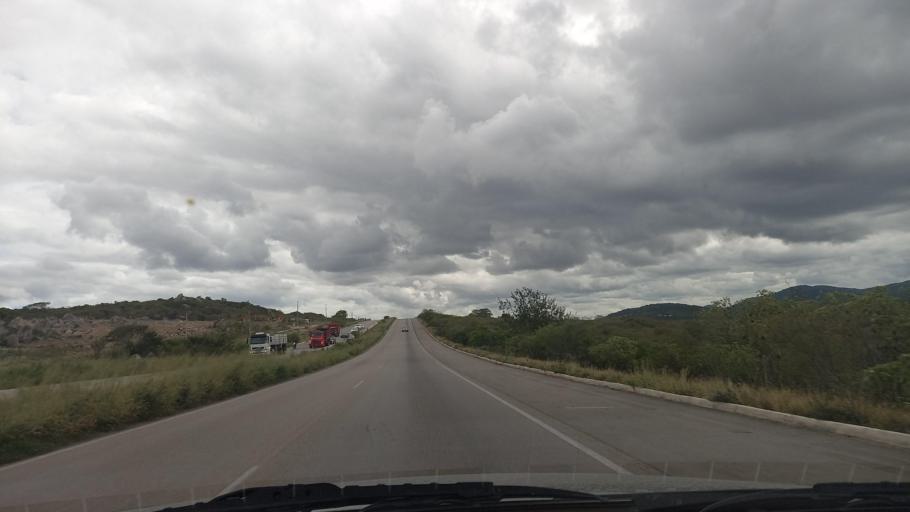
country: BR
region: Pernambuco
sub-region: Caruaru
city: Caruaru
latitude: -8.3233
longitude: -36.1023
